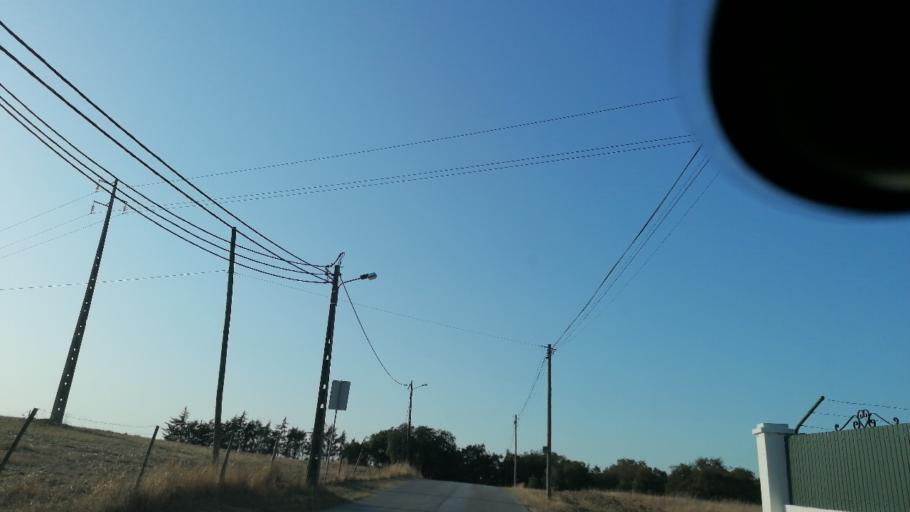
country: PT
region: Setubal
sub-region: Setubal
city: Setubal
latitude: 38.5479
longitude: -8.8415
